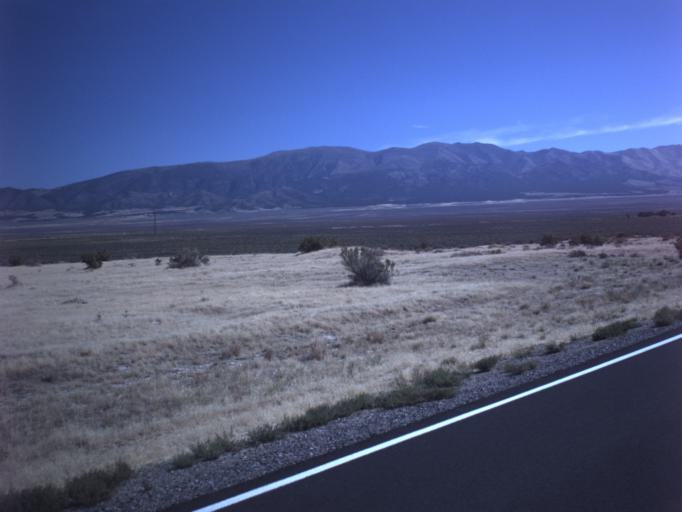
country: US
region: Utah
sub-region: Tooele County
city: Grantsville
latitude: 40.2480
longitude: -112.7263
